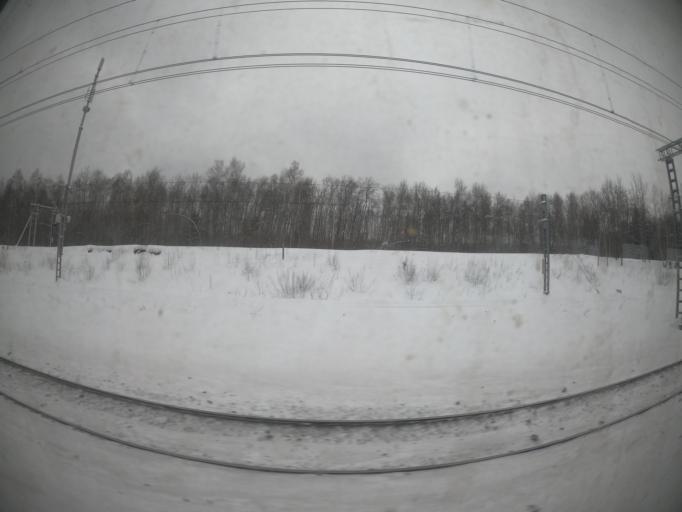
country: RU
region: Moskovskaya
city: Vostryakovo
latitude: 55.4329
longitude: 37.8505
